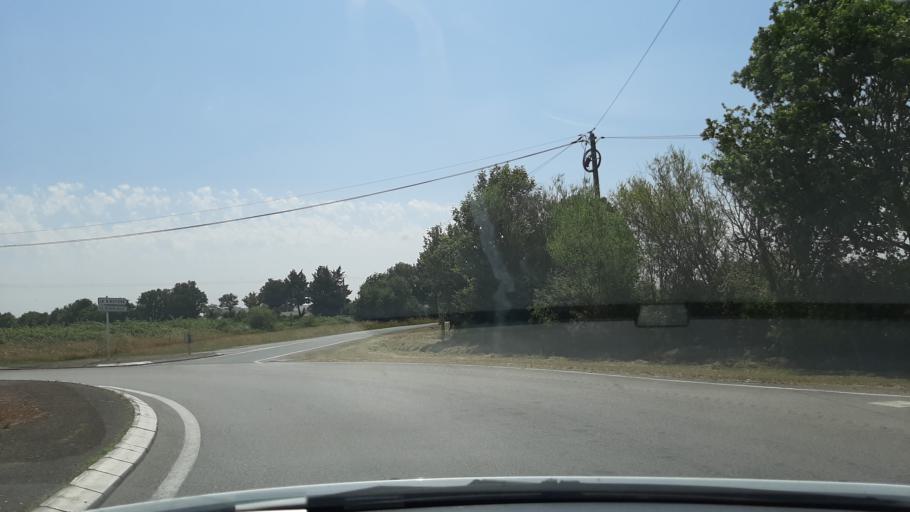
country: FR
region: Pays de la Loire
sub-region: Departement de la Vendee
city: Mouilleron-le-Captif
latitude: 46.7438
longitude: -1.4471
